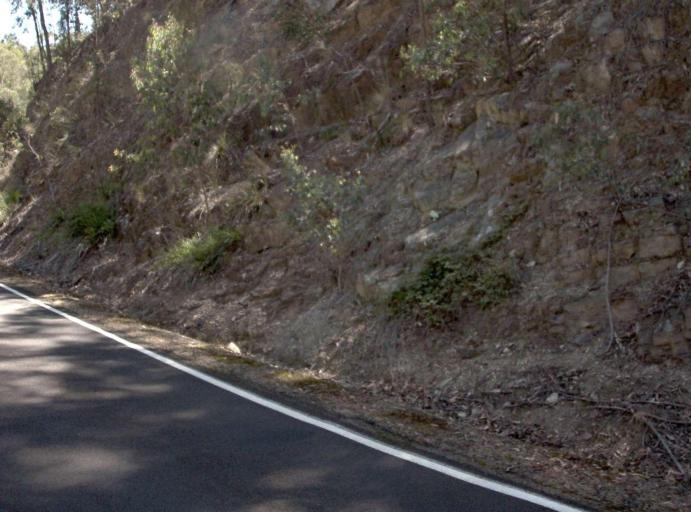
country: AU
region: Victoria
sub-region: East Gippsland
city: Lakes Entrance
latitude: -37.3824
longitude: 148.2187
